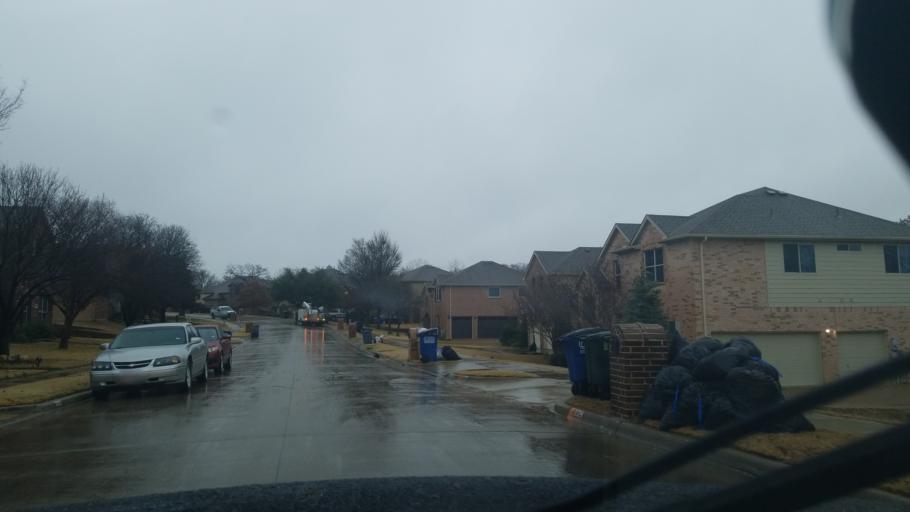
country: US
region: Texas
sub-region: Denton County
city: Corinth
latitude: 33.1346
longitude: -97.0928
